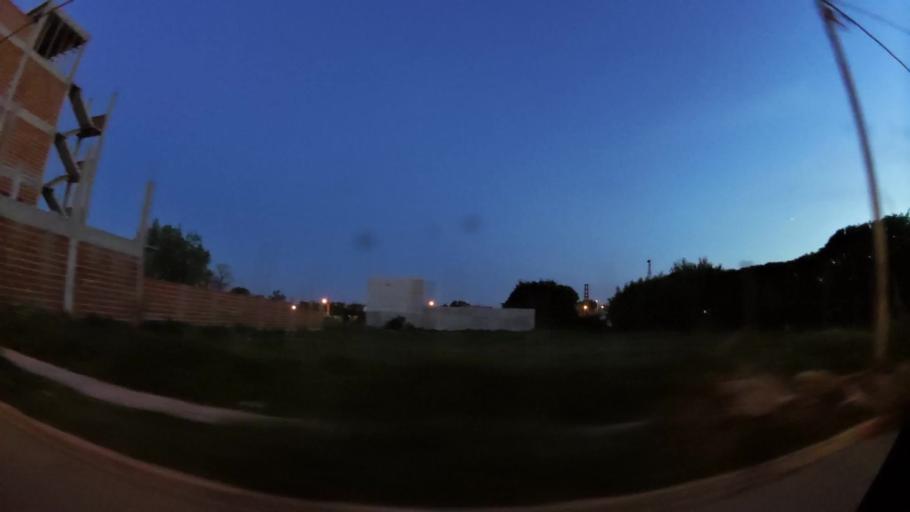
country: AR
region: Buenos Aires
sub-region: Partido de Quilmes
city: Quilmes
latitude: -34.7594
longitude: -58.1950
